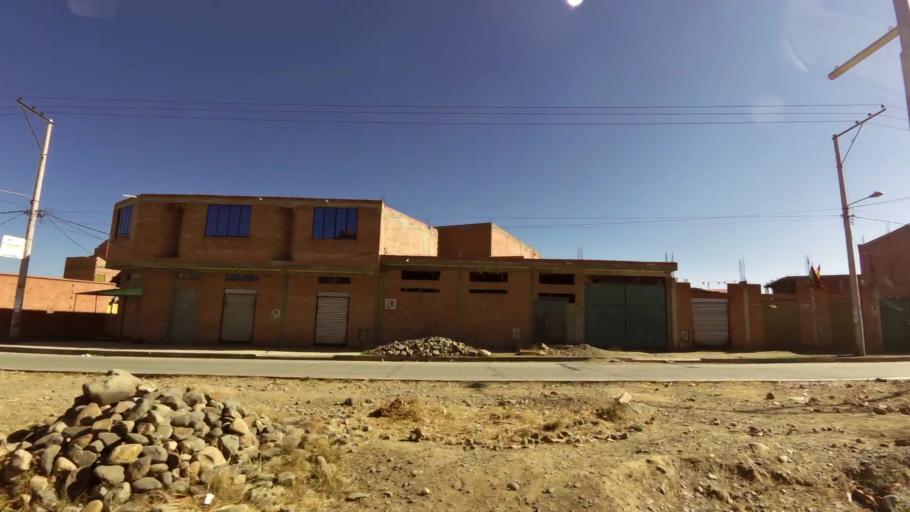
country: BO
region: La Paz
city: La Paz
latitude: -16.5295
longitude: -68.2315
